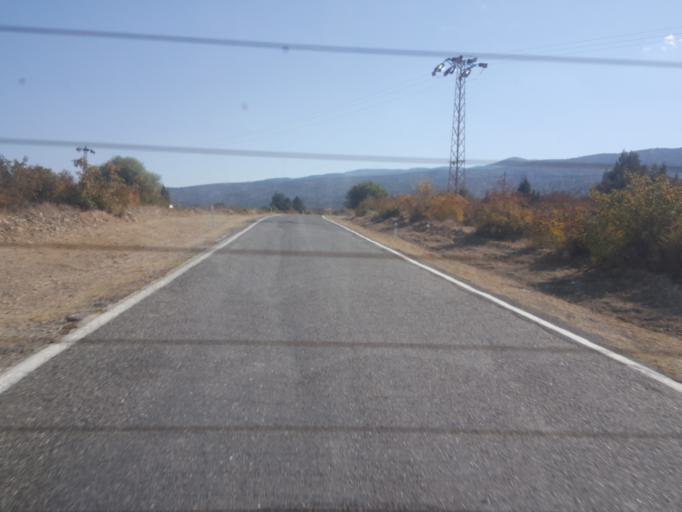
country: TR
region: Kastamonu
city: Tosya
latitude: 41.0016
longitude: 34.1525
